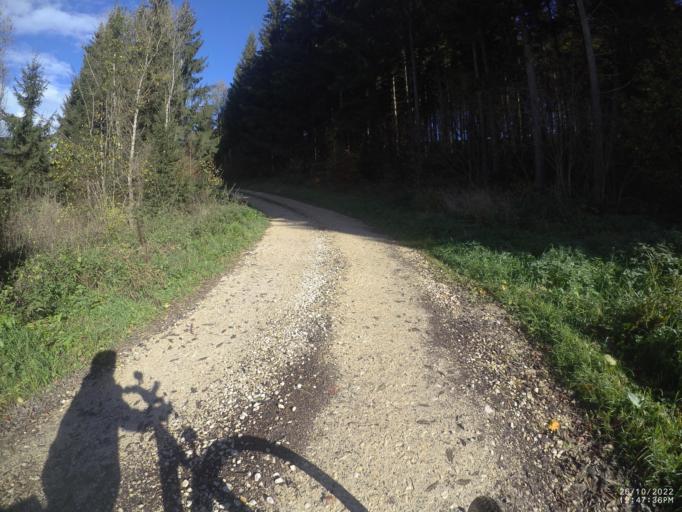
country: DE
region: Baden-Wuerttemberg
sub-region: Regierungsbezirk Stuttgart
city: Wiesensteig
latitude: 48.5394
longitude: 9.6145
